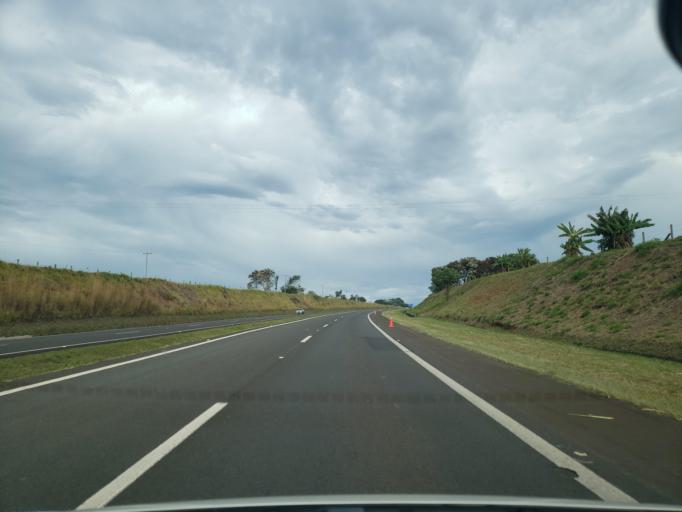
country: BR
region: Sao Paulo
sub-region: Dois Corregos
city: Dois Corregos
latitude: -22.2572
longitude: -48.3661
